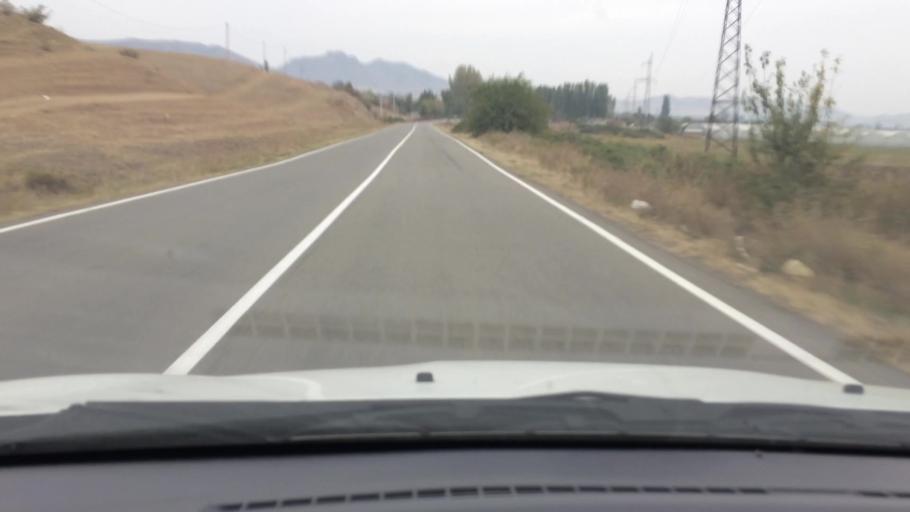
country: AM
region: Tavush
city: Bagratashen
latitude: 41.2880
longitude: 44.7891
